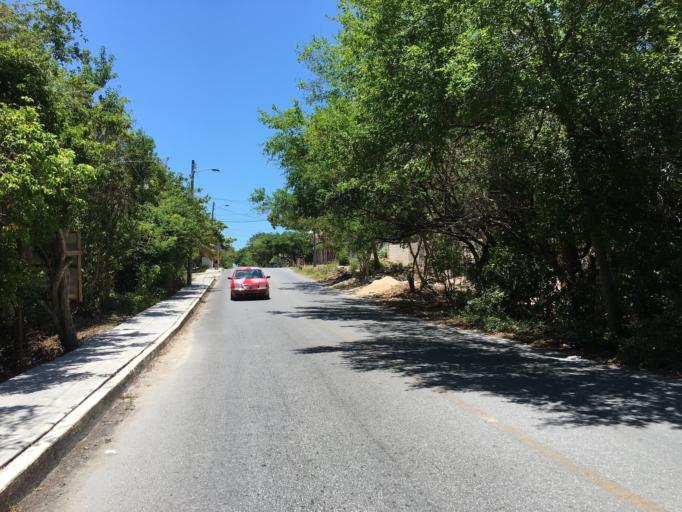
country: MX
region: Quintana Roo
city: Isla Mujeres
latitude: 21.2158
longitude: -86.7247
